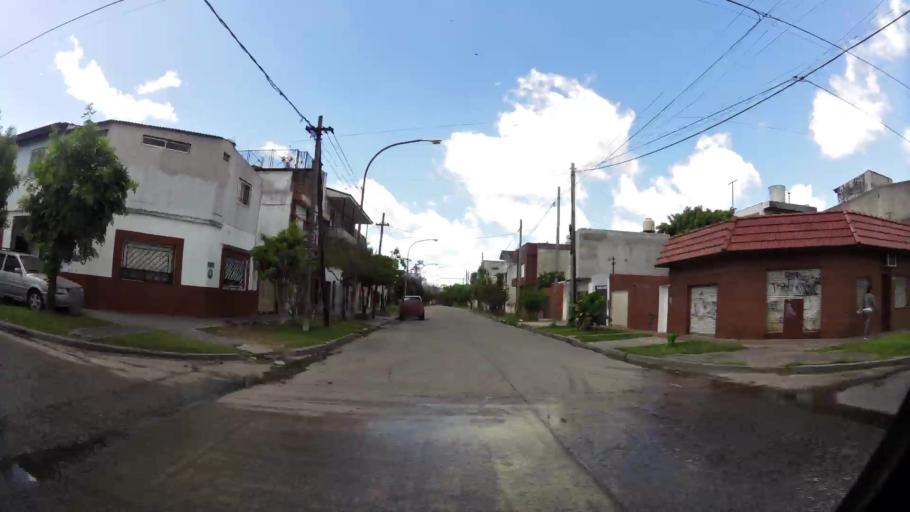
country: AR
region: Buenos Aires
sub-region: Partido de Lanus
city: Lanus
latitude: -34.6942
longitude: -58.4210
